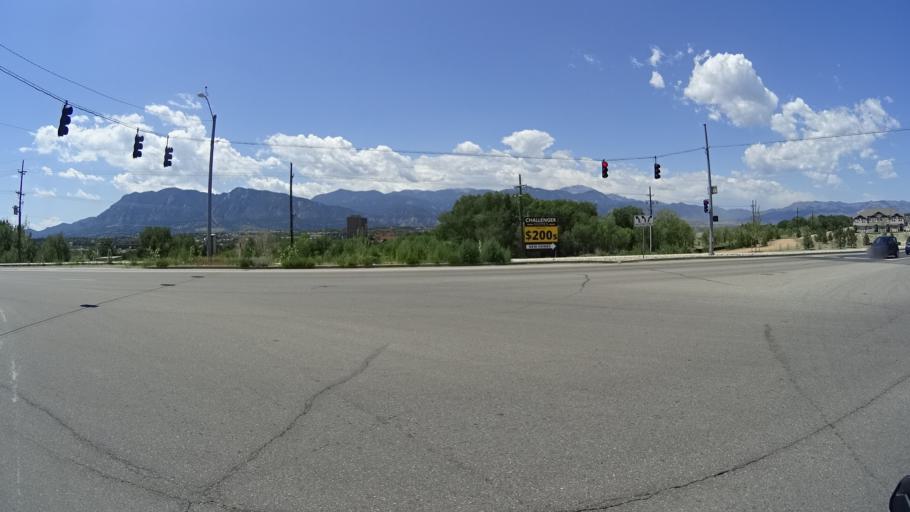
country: US
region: Colorado
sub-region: El Paso County
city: Stratmoor
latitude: 38.7999
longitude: -104.7850
